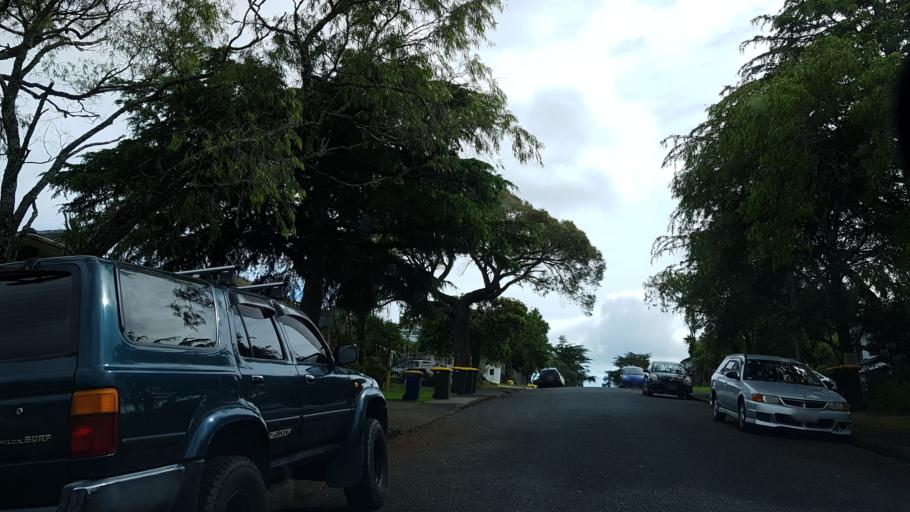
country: NZ
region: Auckland
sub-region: Auckland
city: North Shore
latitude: -36.7913
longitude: 174.7382
